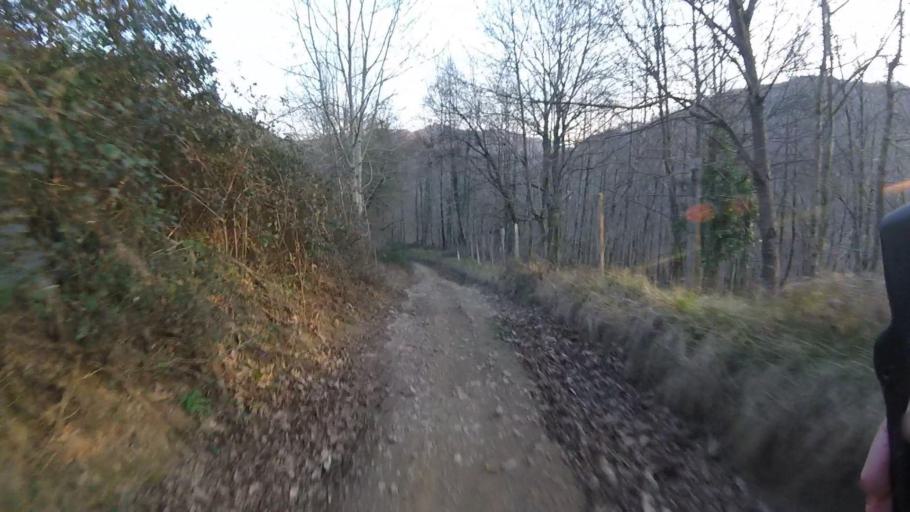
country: ES
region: Basque Country
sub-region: Provincia de Guipuzcoa
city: Errenteria
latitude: 43.2711
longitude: -1.8588
